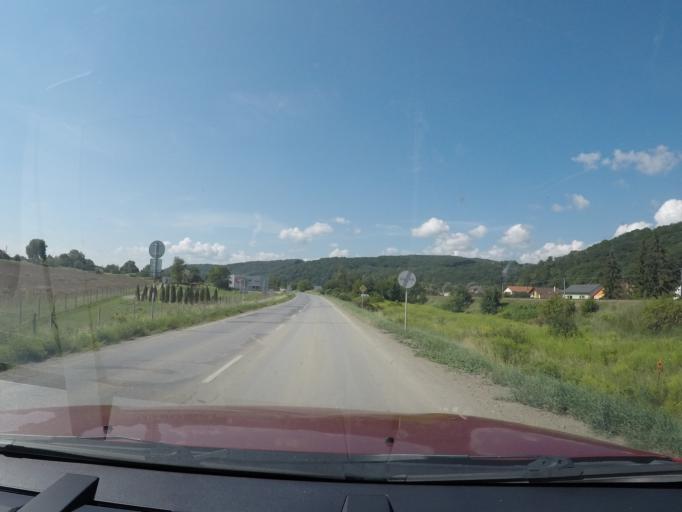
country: SK
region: Presovsky
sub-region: Okres Presov
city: Presov
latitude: 48.9623
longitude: 21.2437
